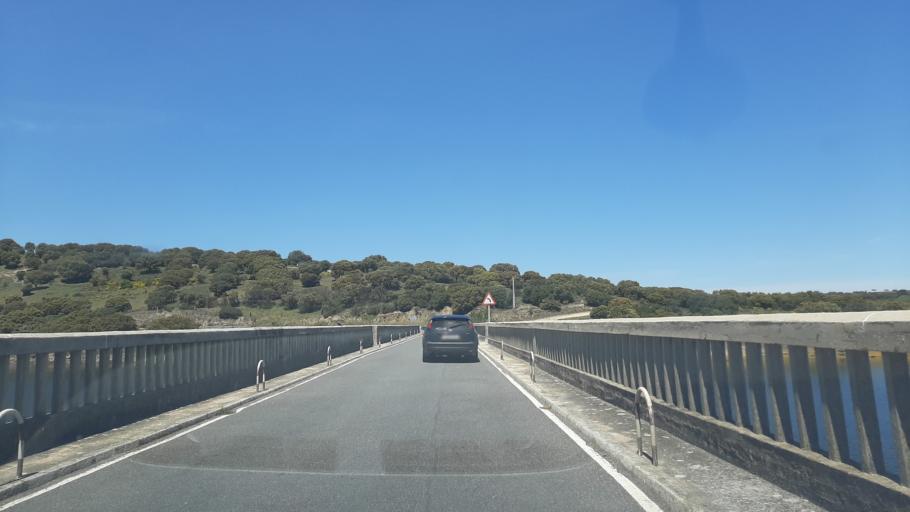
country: ES
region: Castille and Leon
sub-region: Provincia de Salamanca
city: Guijo de Avila
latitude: 40.5532
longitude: -5.6293
